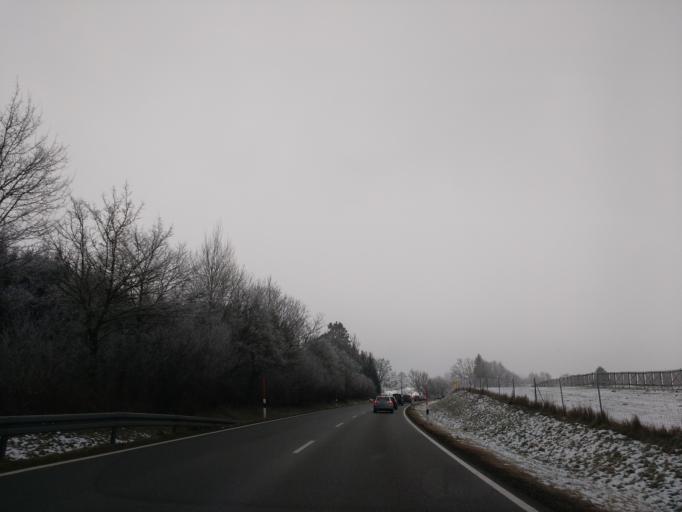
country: DE
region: Bavaria
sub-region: Swabia
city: Oy-Mittelberg
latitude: 47.6406
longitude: 10.4693
